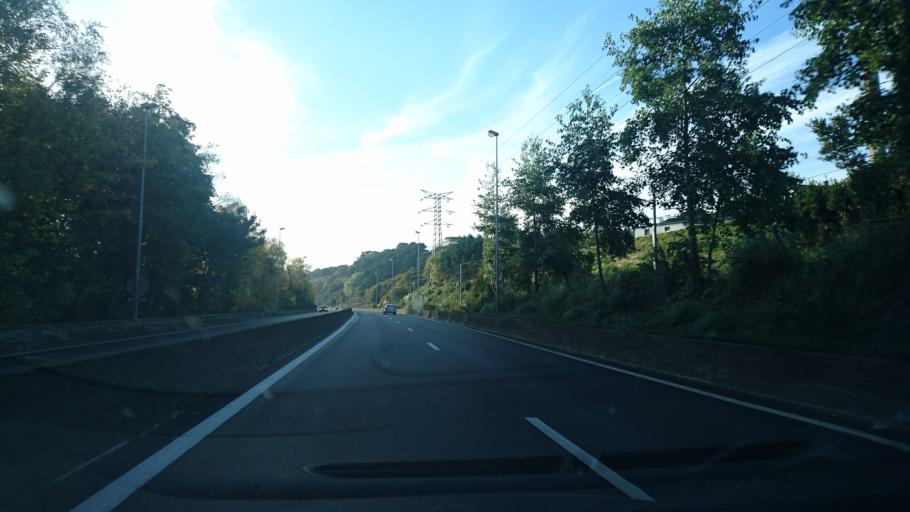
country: FR
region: Brittany
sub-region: Departement du Finistere
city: Brest
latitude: 48.3936
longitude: -4.4448
